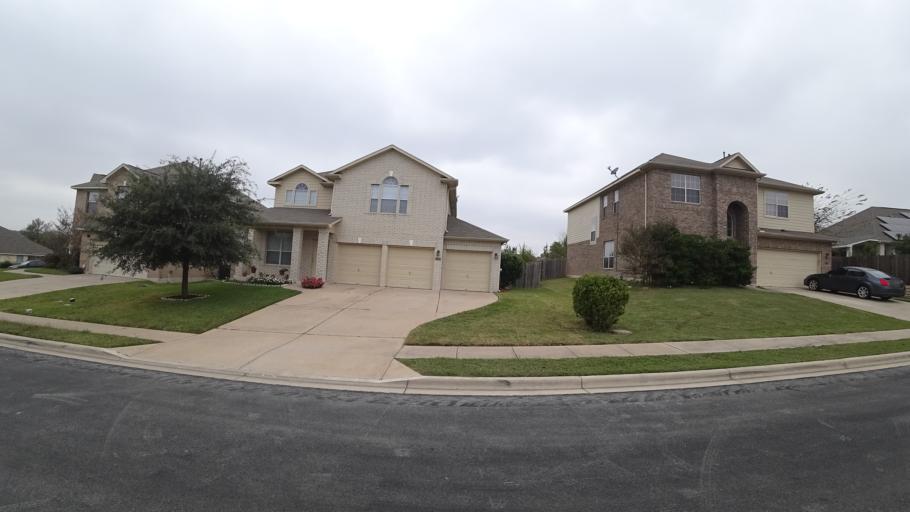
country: US
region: Texas
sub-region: Travis County
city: Pflugerville
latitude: 30.3712
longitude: -97.6523
